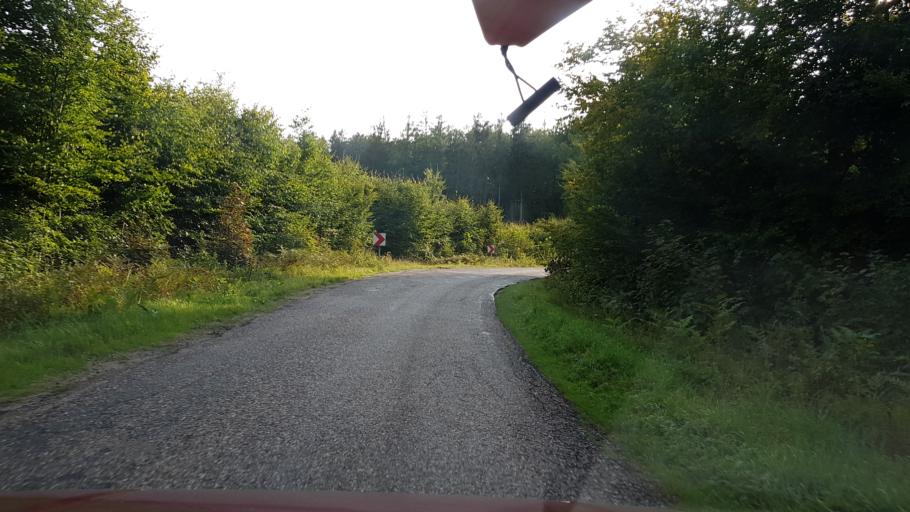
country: PL
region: Pomeranian Voivodeship
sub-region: Powiat bytowski
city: Miastko
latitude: 53.9840
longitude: 16.8969
